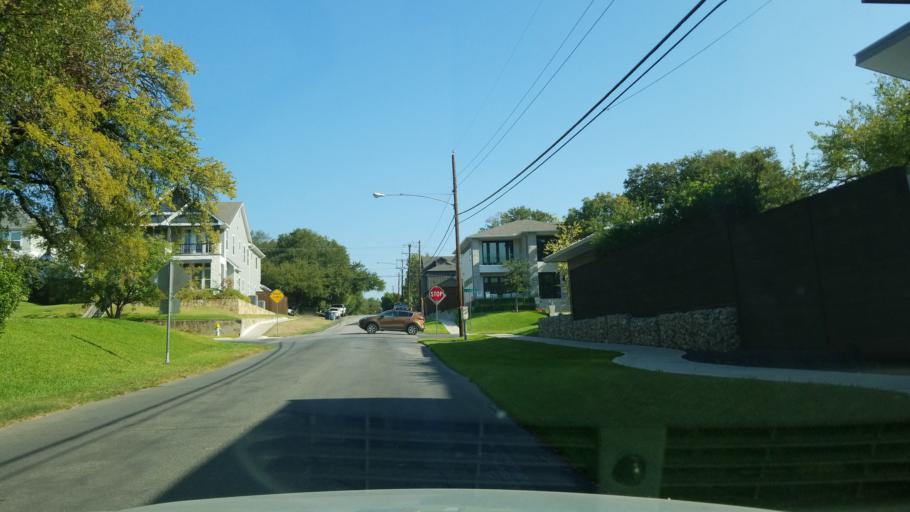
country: US
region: Texas
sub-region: Dallas County
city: Highland Park
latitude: 32.8104
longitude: -96.7388
